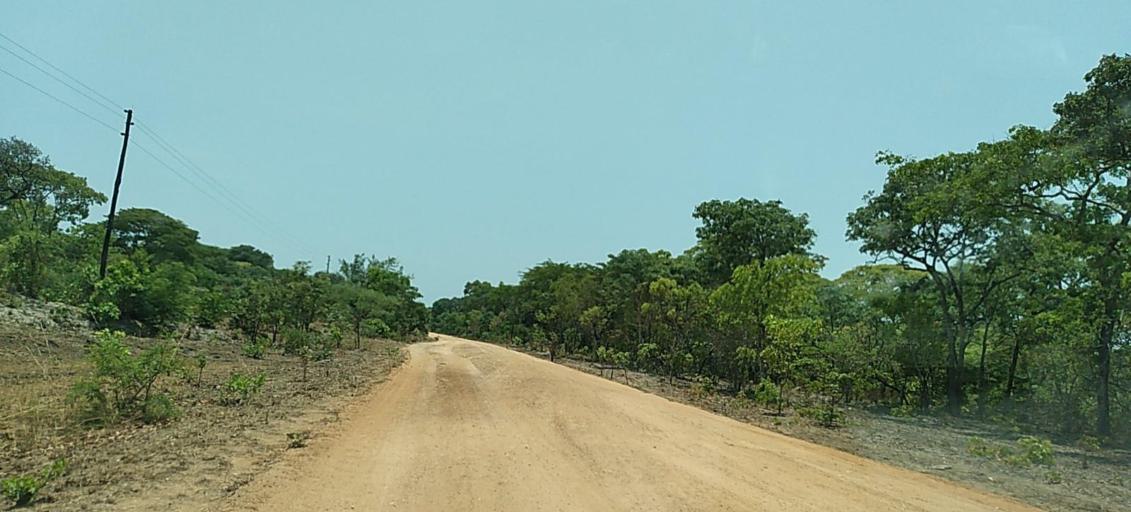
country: ZM
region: Copperbelt
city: Mpongwe
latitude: -13.8017
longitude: 27.8592
